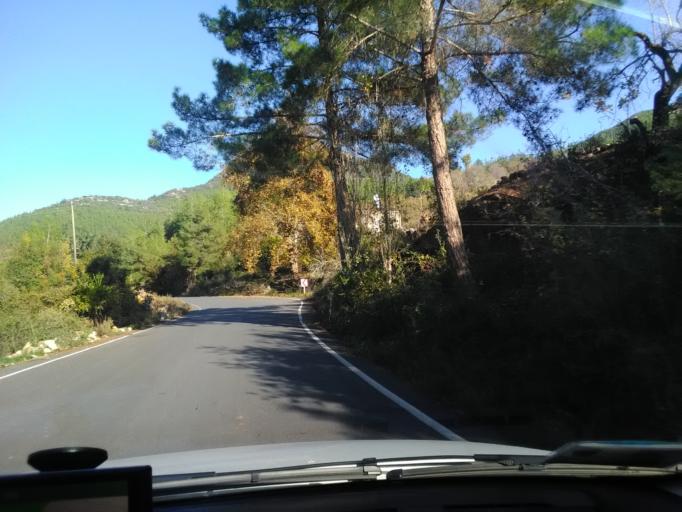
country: TR
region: Antalya
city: Gazipasa
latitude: 36.2850
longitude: 32.3721
